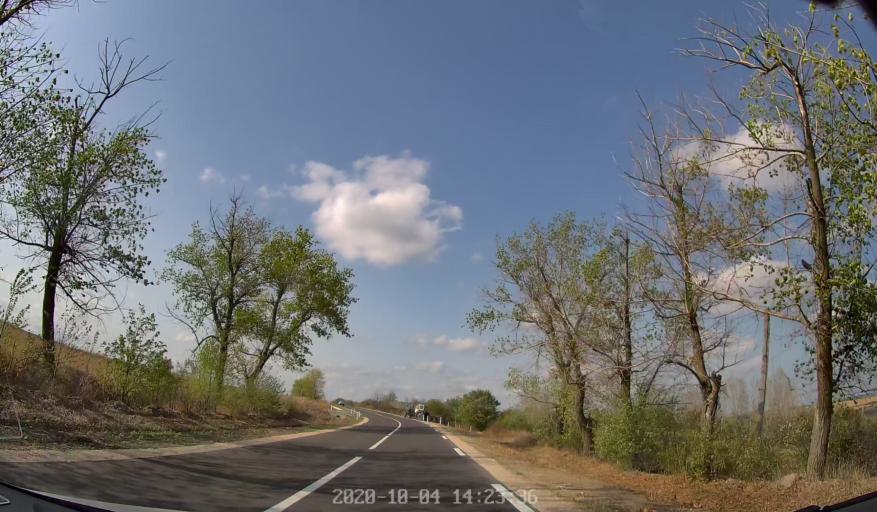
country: MD
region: Rezina
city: Saharna
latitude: 47.6097
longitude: 28.9327
